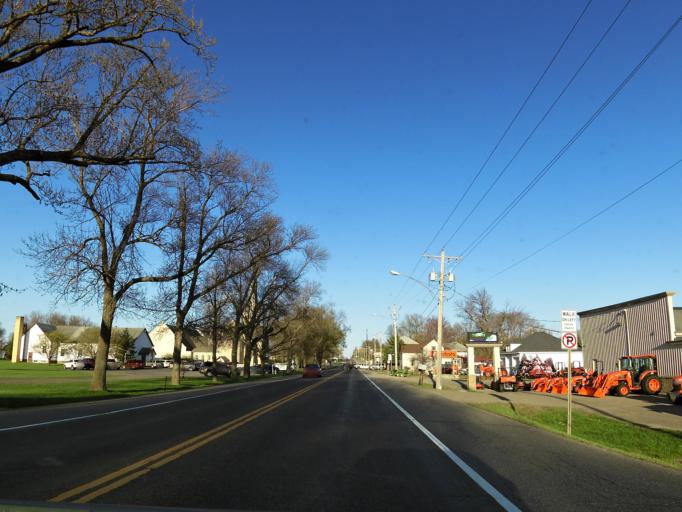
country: US
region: Minnesota
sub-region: Goodhue County
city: Cannon Falls
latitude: 44.6006
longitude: -92.8155
